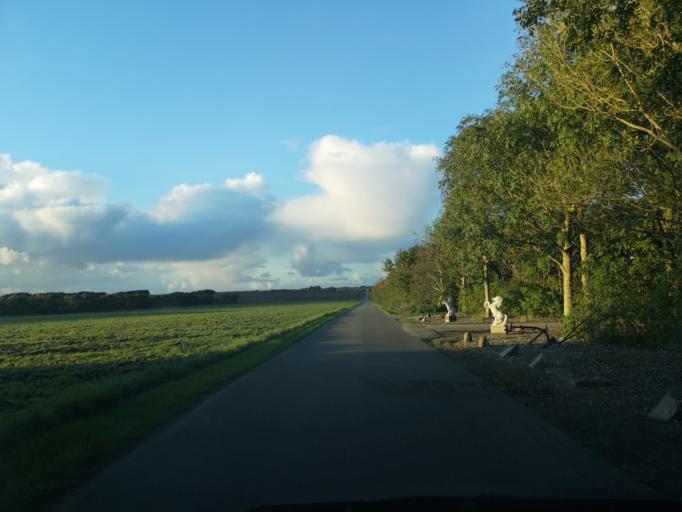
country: DK
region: Central Jutland
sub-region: Ringkobing-Skjern Kommune
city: Videbaek
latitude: 56.0318
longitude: 8.5741
